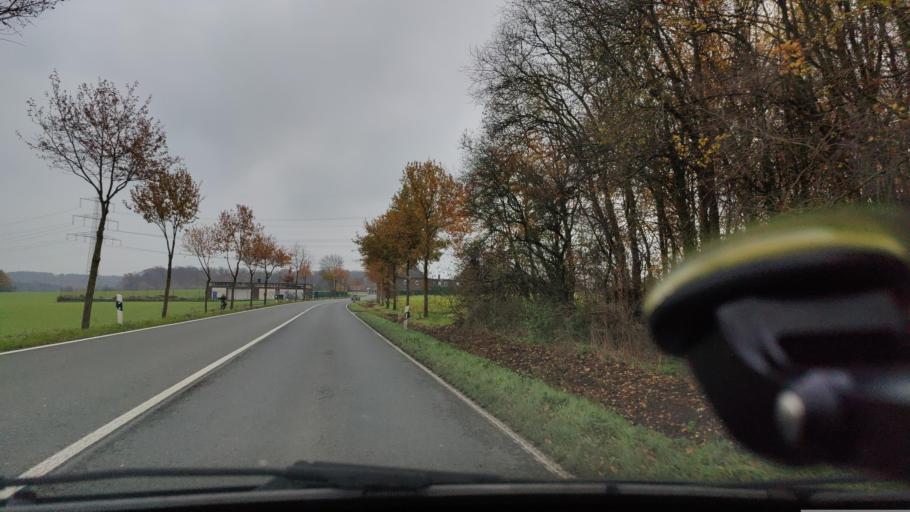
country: DE
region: North Rhine-Westphalia
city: Selm
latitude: 51.6615
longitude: 7.4928
